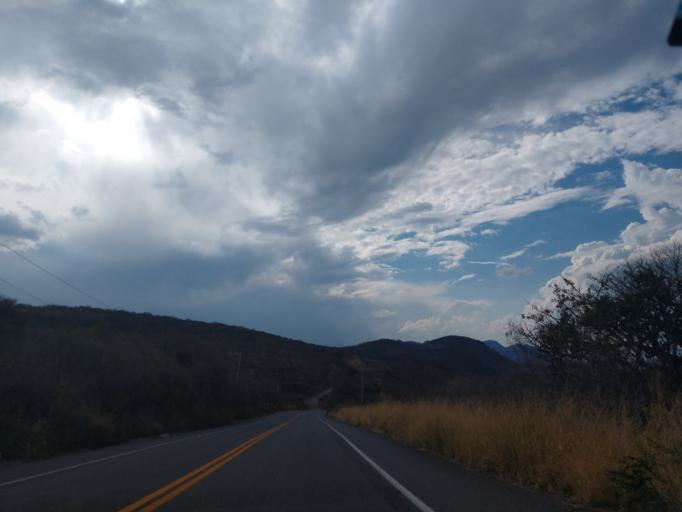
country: MX
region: Jalisco
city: Tizapan el Alto
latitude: 20.1247
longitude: -103.1564
